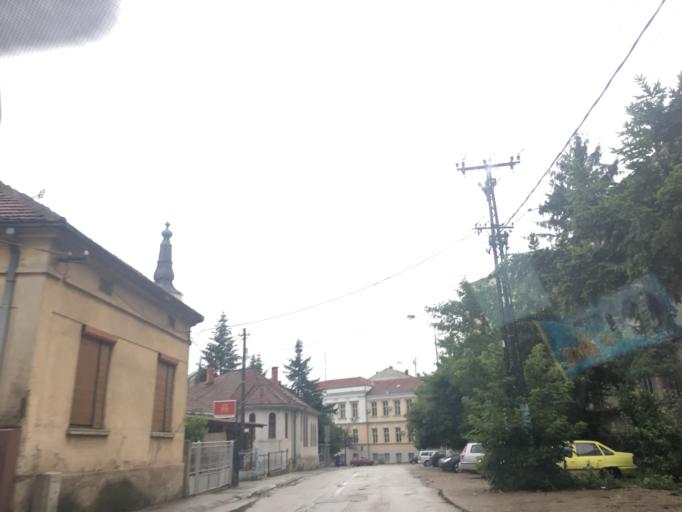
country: RS
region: Central Serbia
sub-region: Nisavski Okrug
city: Aleksinac
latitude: 43.5431
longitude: 21.7071
